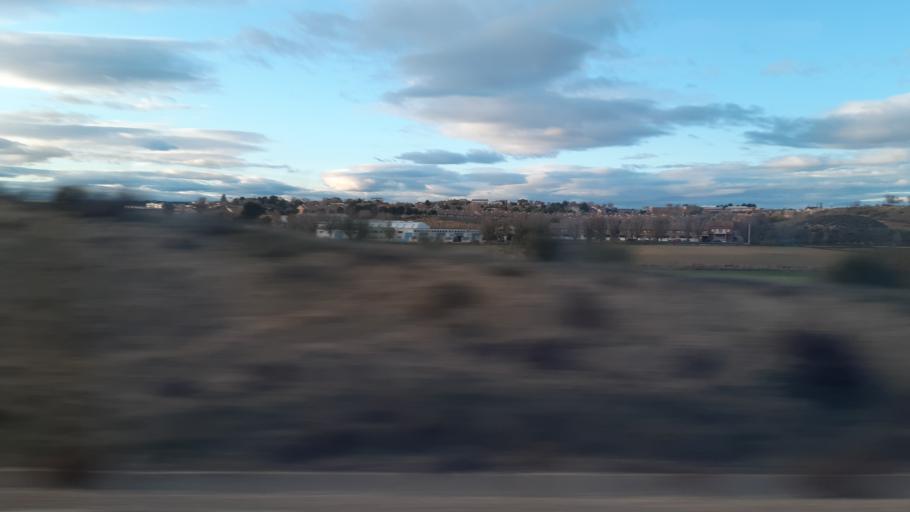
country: ES
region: Madrid
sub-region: Provincia de Madrid
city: Torres de la Alameda
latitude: 40.4396
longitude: -3.3460
